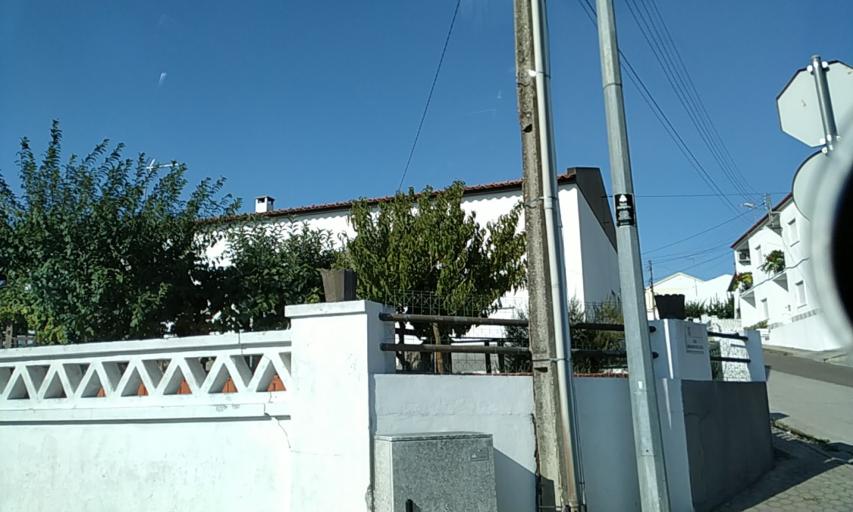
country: PT
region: Santarem
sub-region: Coruche
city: Coruche
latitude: 38.9644
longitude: -8.5333
